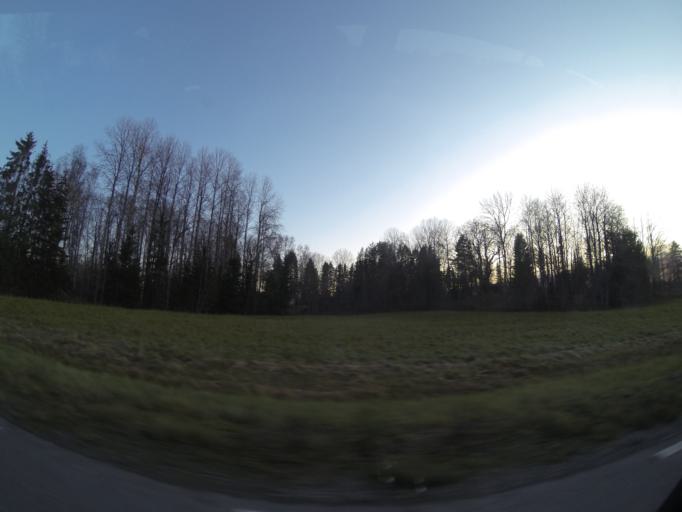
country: SE
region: OErebro
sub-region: Orebro Kommun
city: Hovsta
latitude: 59.3136
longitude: 15.2820
